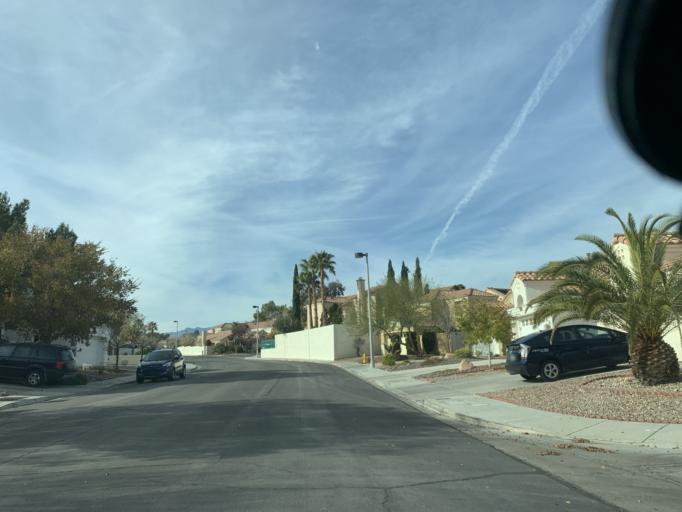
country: US
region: Nevada
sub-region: Clark County
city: Summerlin South
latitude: 36.1496
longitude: -115.2982
